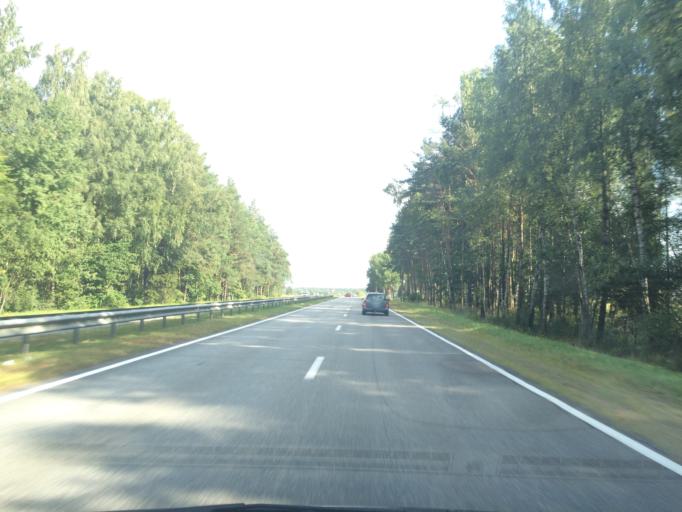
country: LV
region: Ikskile
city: Ikskile
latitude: 56.8250
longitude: 24.5286
